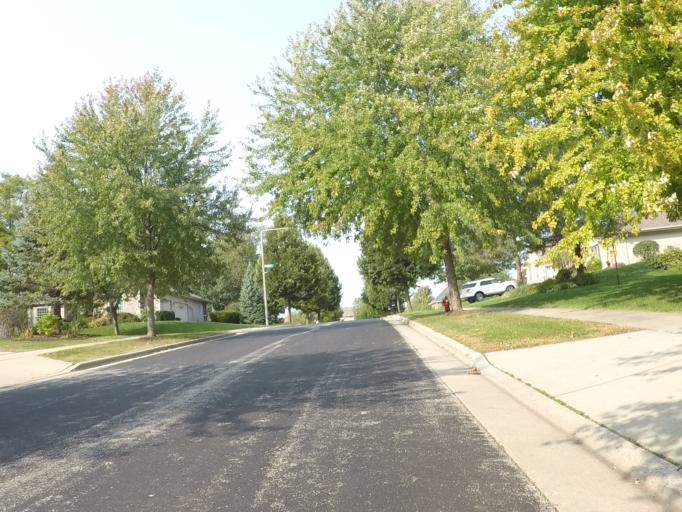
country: US
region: Wisconsin
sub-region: Dane County
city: Verona
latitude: 43.0349
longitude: -89.5381
